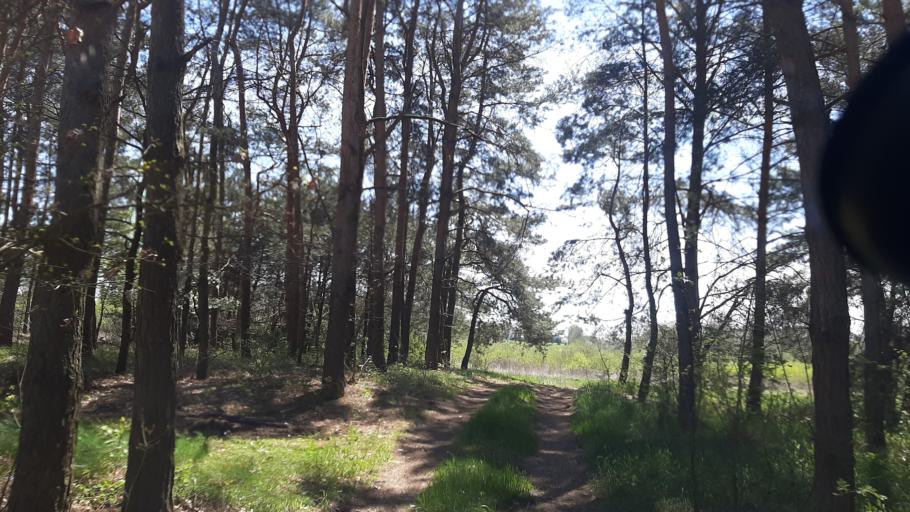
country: PL
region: Lublin Voivodeship
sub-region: Powiat lubelski
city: Garbow
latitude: 51.4026
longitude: 22.3168
